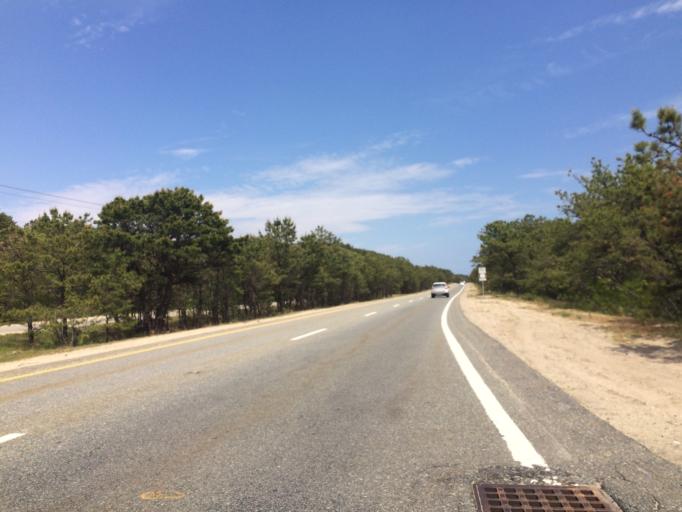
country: US
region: Massachusetts
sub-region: Barnstable County
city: Provincetown
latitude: 42.0625
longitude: -70.1806
